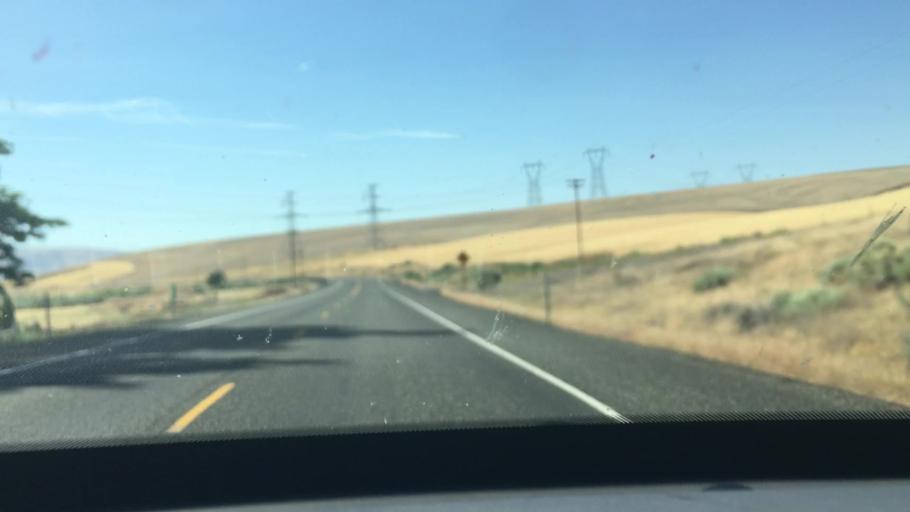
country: US
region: Oregon
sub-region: Sherman County
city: Moro
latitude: 45.6239
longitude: -120.7461
